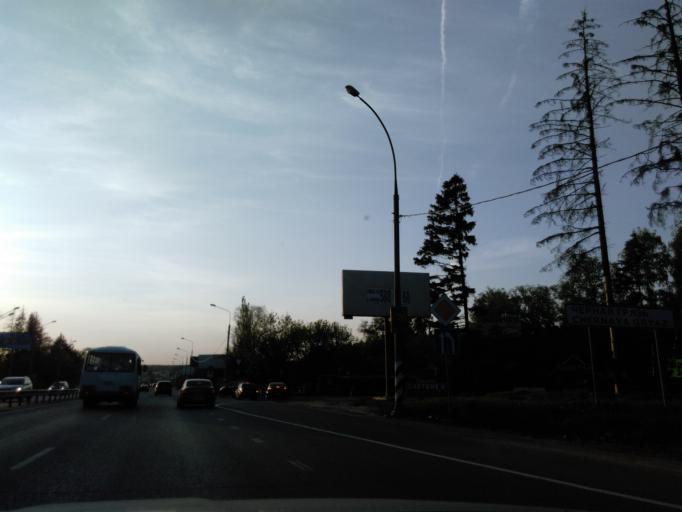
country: RU
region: Moskovskaya
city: Skhodnya
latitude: 55.9684
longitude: 37.3240
